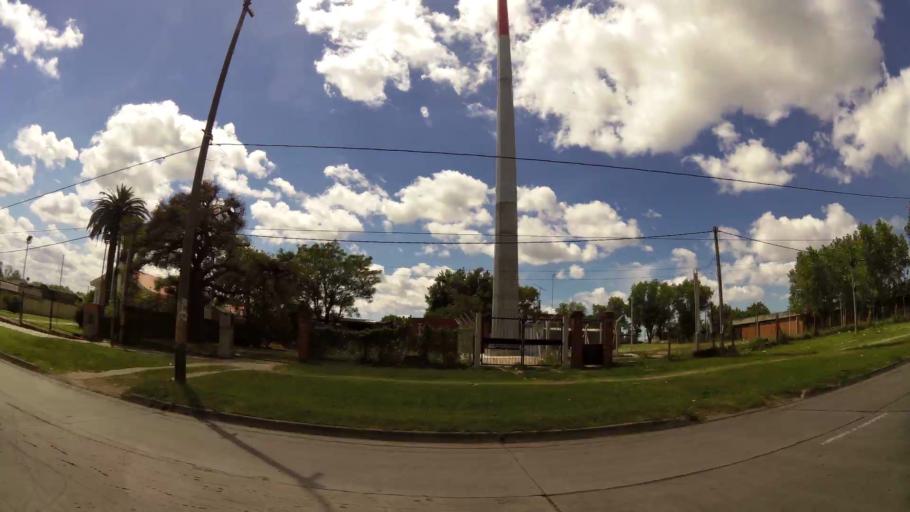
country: UY
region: Canelones
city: Paso de Carrasco
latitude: -34.8307
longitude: -56.1100
